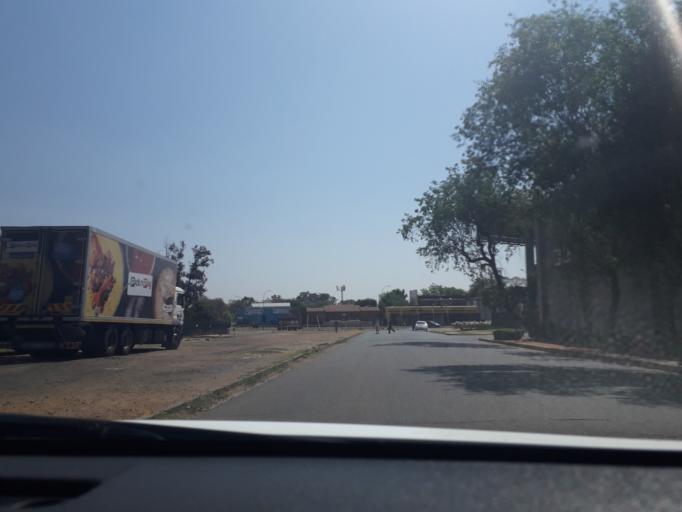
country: ZA
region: Gauteng
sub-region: City of Johannesburg Metropolitan Municipality
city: Roodepoort
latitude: -26.1276
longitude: 27.9668
